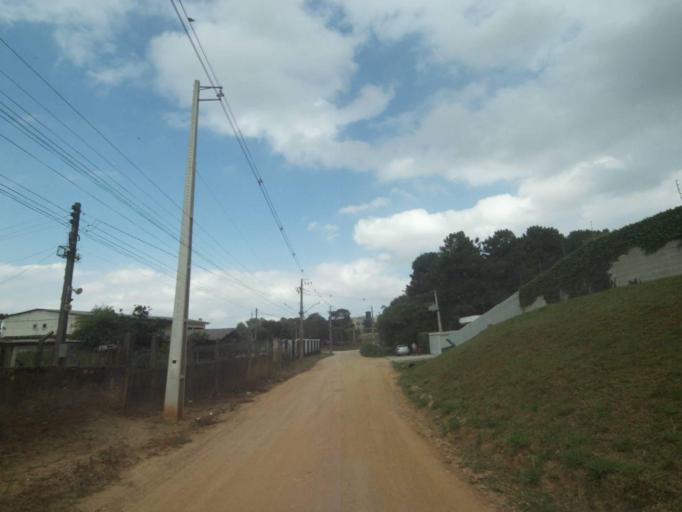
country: BR
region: Parana
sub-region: Araucaria
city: Araucaria
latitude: -25.5166
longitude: -49.3453
